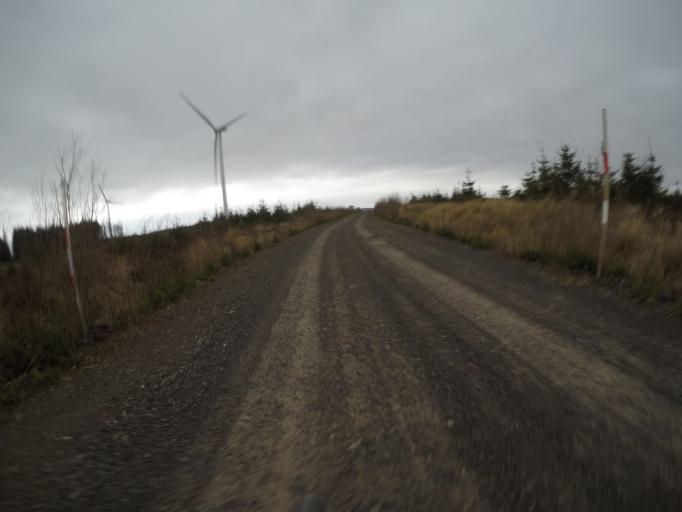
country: GB
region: Scotland
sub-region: East Ayrshire
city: Newmilns
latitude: 55.6775
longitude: -4.3439
